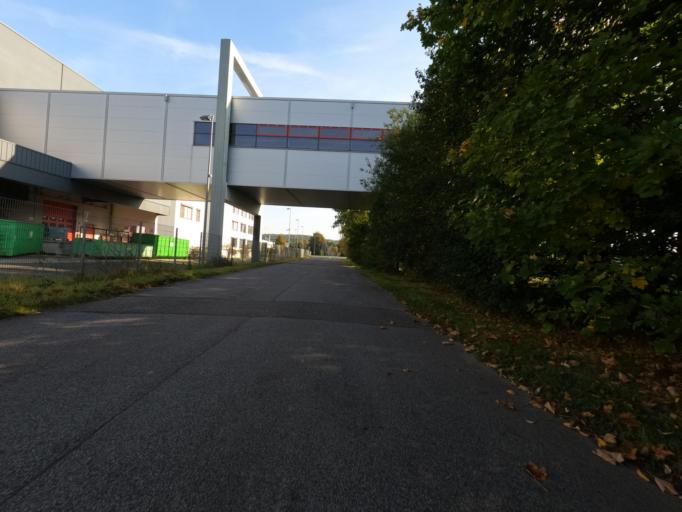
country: DE
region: North Rhine-Westphalia
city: Huckelhoven
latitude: 51.0362
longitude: 6.2531
